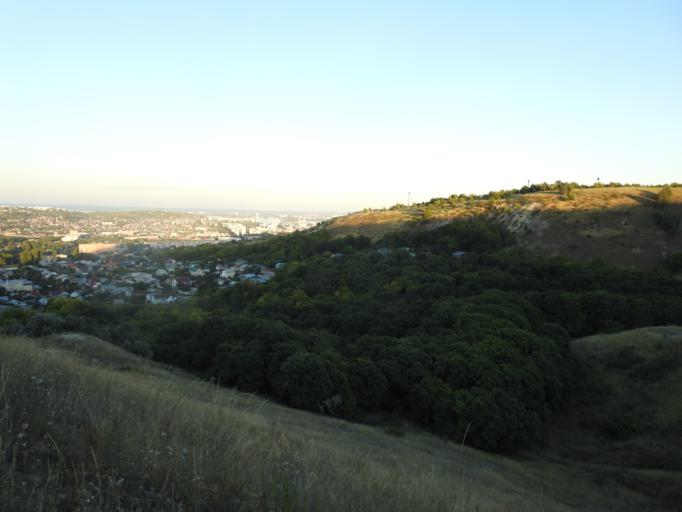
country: RU
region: Saratov
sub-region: Saratovskiy Rayon
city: Saratov
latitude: 51.5565
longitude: 45.9780
